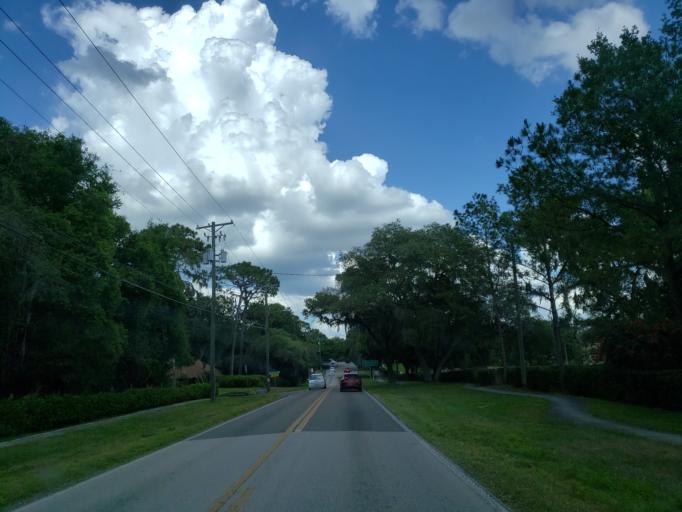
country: US
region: Florida
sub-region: Hillsborough County
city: Mango
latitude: 27.9523
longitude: -82.3135
